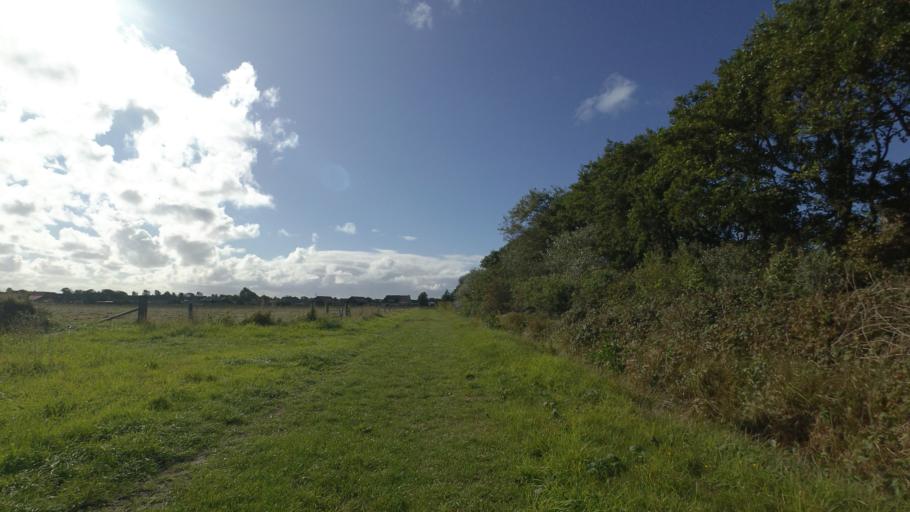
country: NL
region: Friesland
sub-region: Gemeente Ameland
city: Nes
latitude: 53.4512
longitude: 5.8067
